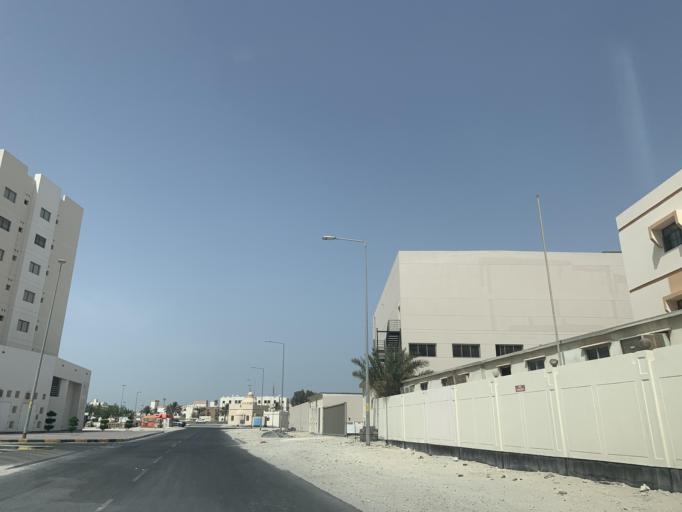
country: BH
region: Northern
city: Madinat `Isa
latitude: 26.1557
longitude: 50.5657
